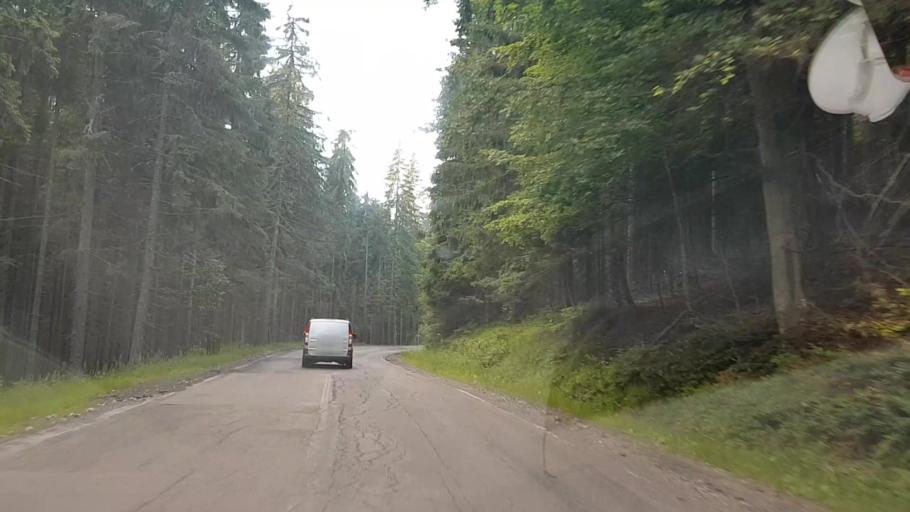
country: RO
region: Harghita
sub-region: Comuna Varsag
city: Varsag
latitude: 46.6584
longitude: 25.2997
